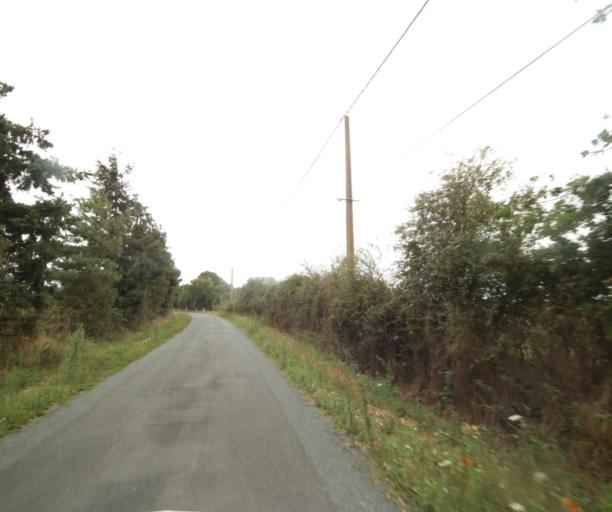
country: FR
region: Pays de la Loire
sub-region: Departement de la Sarthe
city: Vion
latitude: 47.8463
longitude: -0.2468
